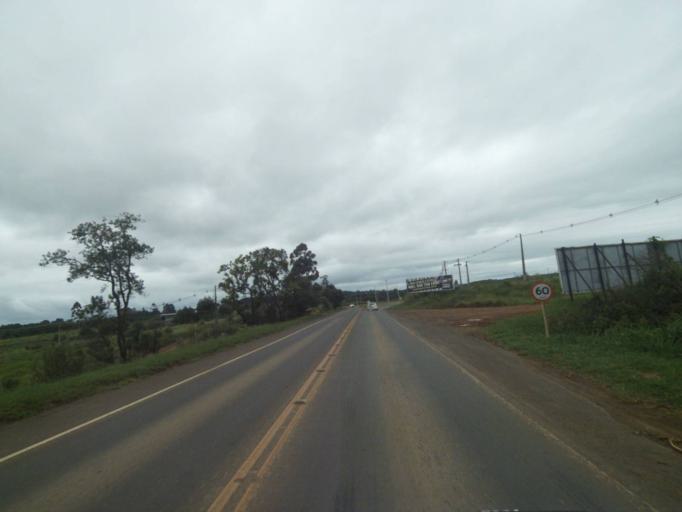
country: BR
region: Parana
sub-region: Telemaco Borba
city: Telemaco Borba
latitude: -24.3854
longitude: -50.6775
